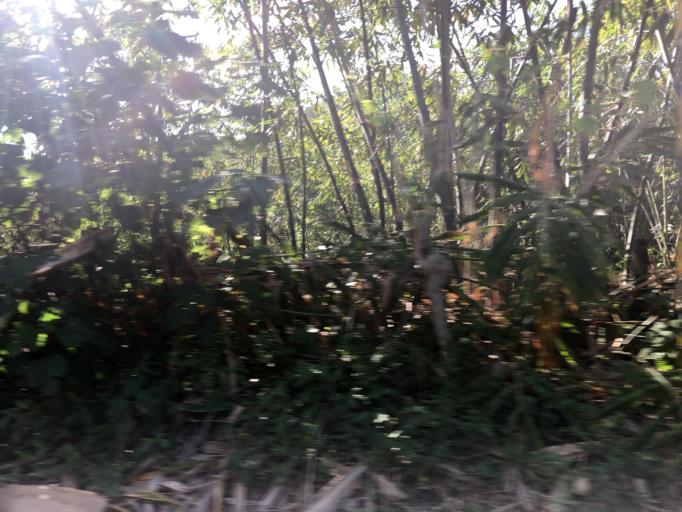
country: TW
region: Taiwan
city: Yujing
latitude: 23.0115
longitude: 120.3856
